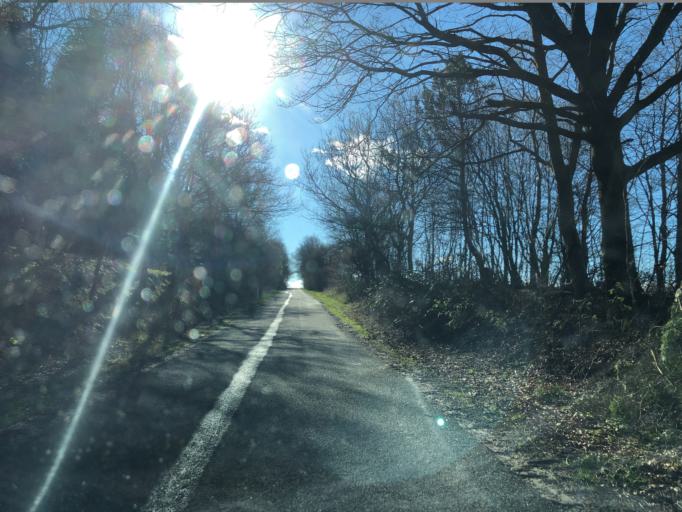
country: DK
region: Central Jutland
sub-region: Favrskov Kommune
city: Hammel
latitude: 56.3198
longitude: 9.8892
